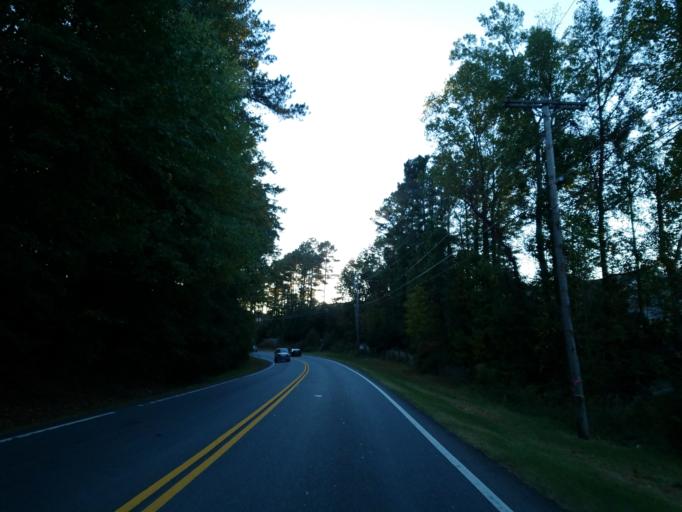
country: US
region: Georgia
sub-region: Forsyth County
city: Cumming
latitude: 34.1795
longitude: -84.1552
